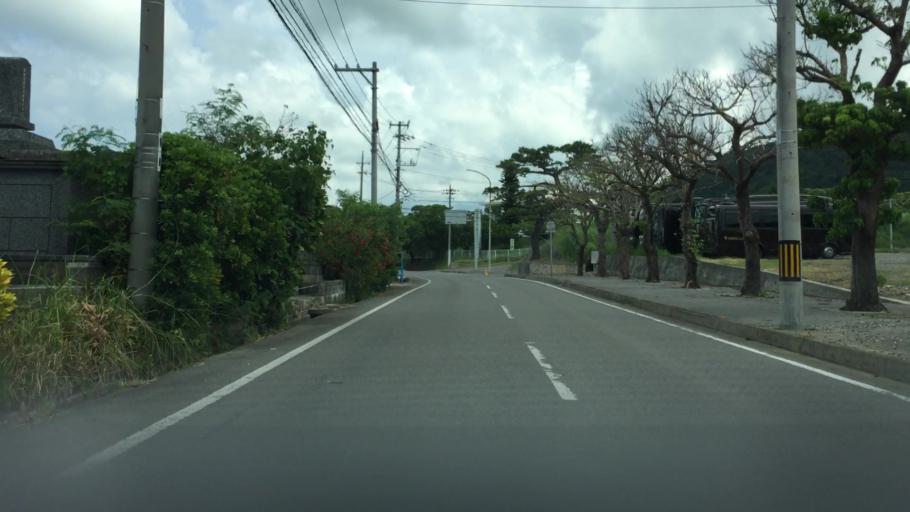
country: JP
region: Okinawa
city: Ishigaki
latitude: 24.3637
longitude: 124.1422
